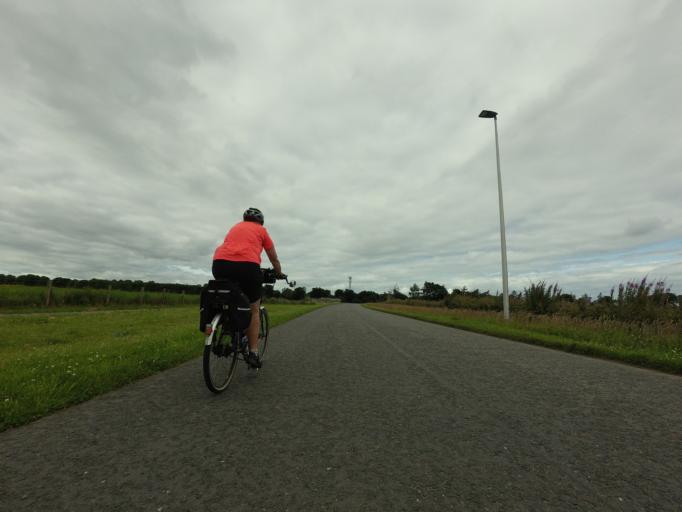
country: GB
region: Scotland
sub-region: Moray
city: Forres
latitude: 57.6138
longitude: -3.6255
